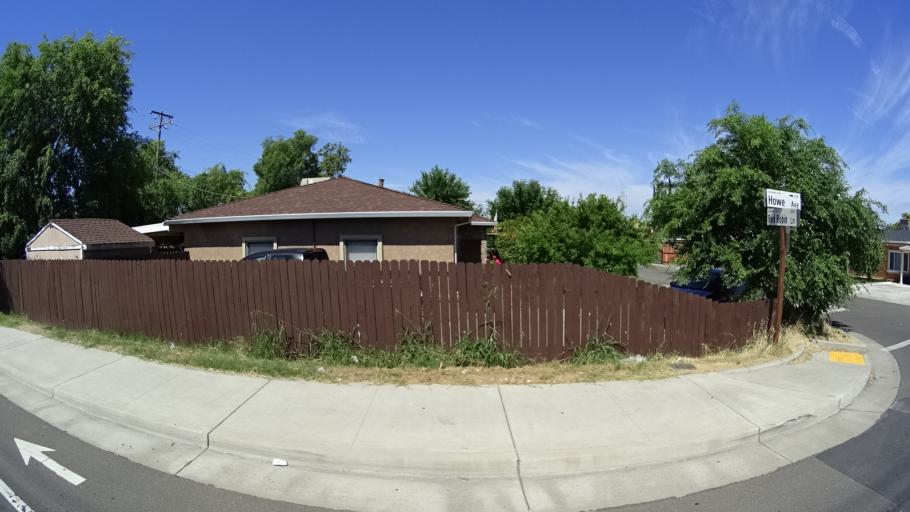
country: US
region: California
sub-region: Sacramento County
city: Arden-Arcade
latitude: 38.6153
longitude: -121.4154
